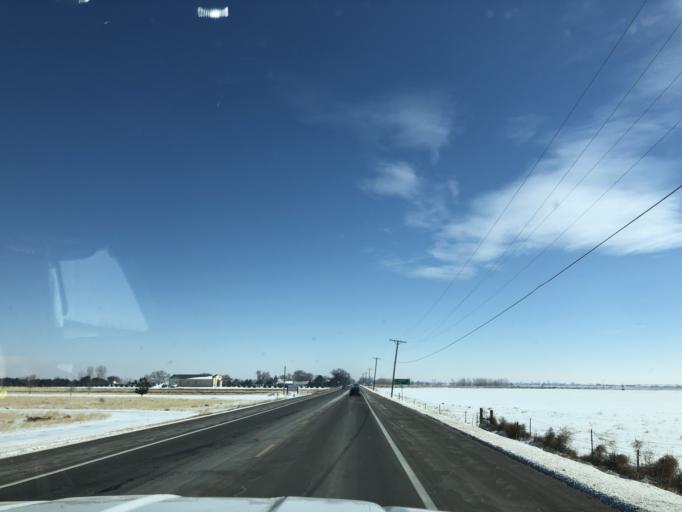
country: US
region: Colorado
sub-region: Morgan County
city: Fort Morgan
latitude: 40.2542
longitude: -103.8740
